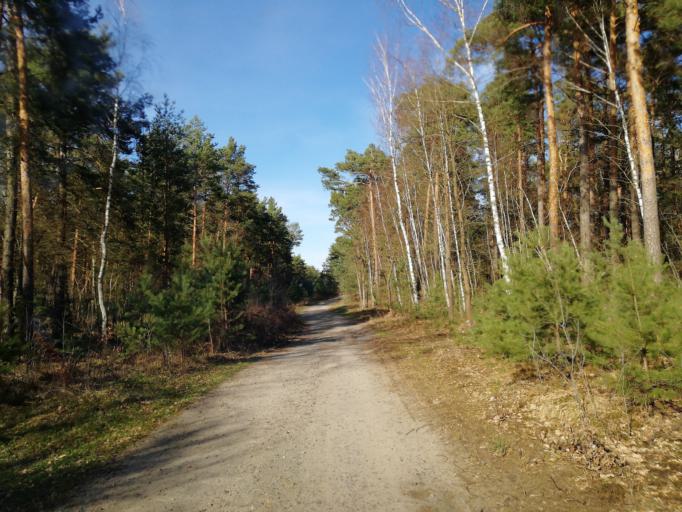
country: DE
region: Brandenburg
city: Ruckersdorf
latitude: 51.5626
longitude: 13.5908
